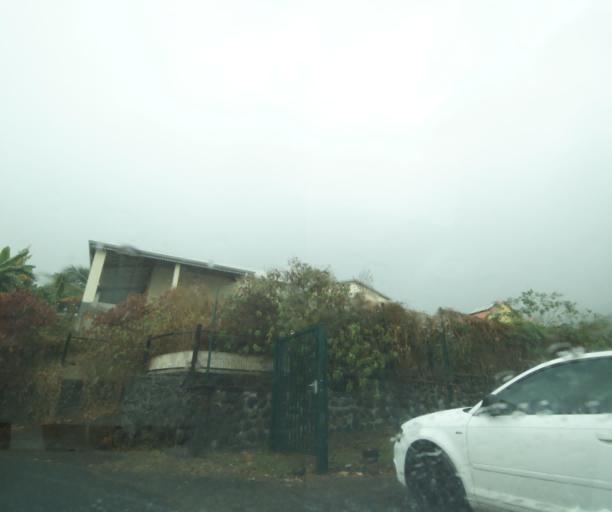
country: RE
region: Reunion
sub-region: Reunion
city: La Possession
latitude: -20.9804
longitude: 55.3373
